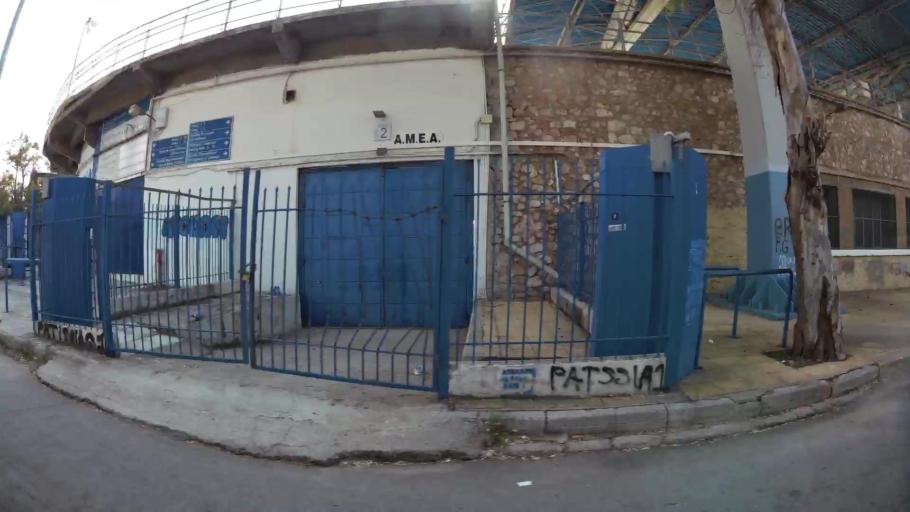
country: GR
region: Attica
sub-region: Nomarchia Athinas
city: Nea Filadelfeia
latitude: 38.0284
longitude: 23.7418
